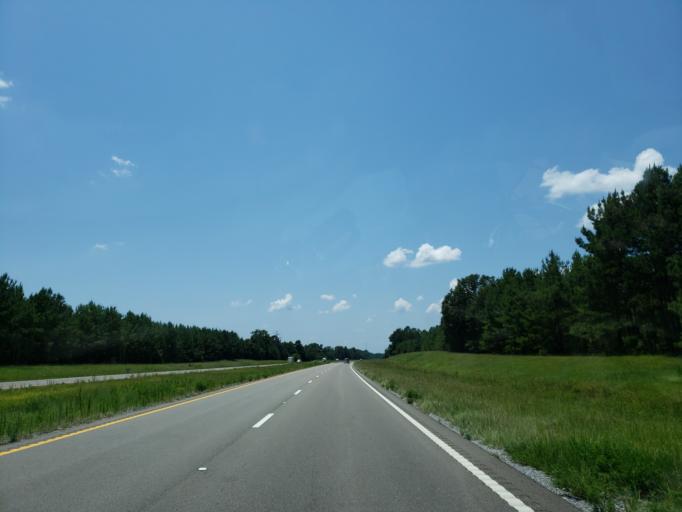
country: US
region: Mississippi
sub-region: Clarke County
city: Quitman
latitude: 31.9955
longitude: -88.6989
